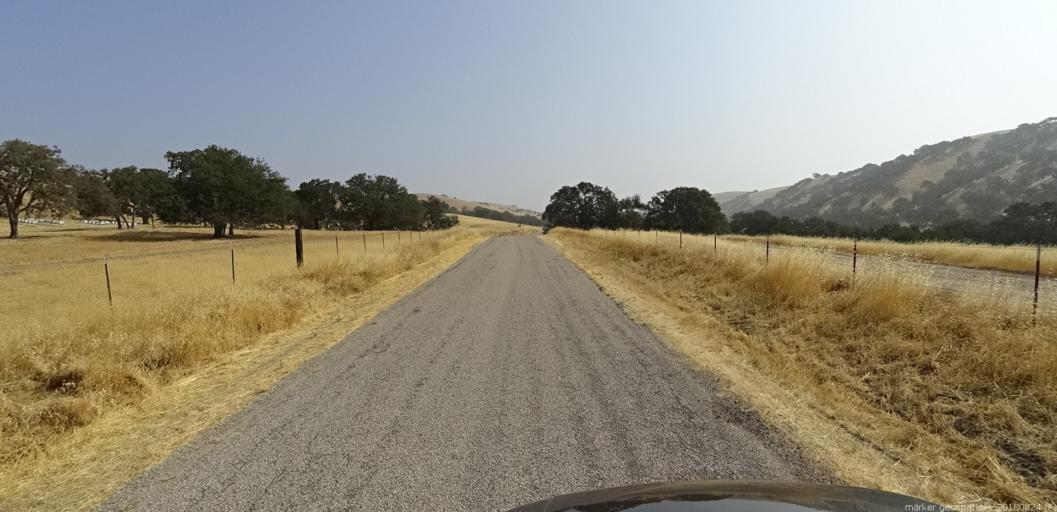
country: US
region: California
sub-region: San Luis Obispo County
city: San Miguel
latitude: 35.8667
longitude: -120.7607
